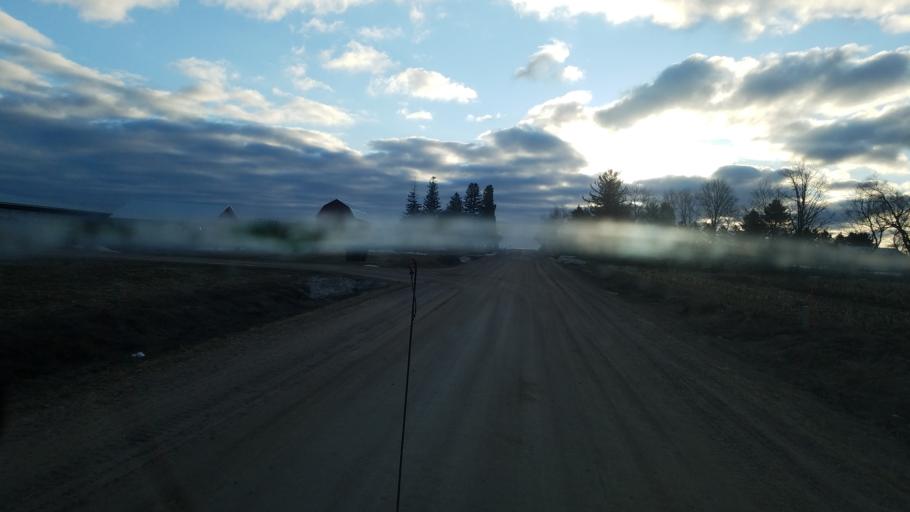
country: US
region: Wisconsin
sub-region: Clark County
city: Loyal
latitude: 44.6110
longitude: -90.4455
